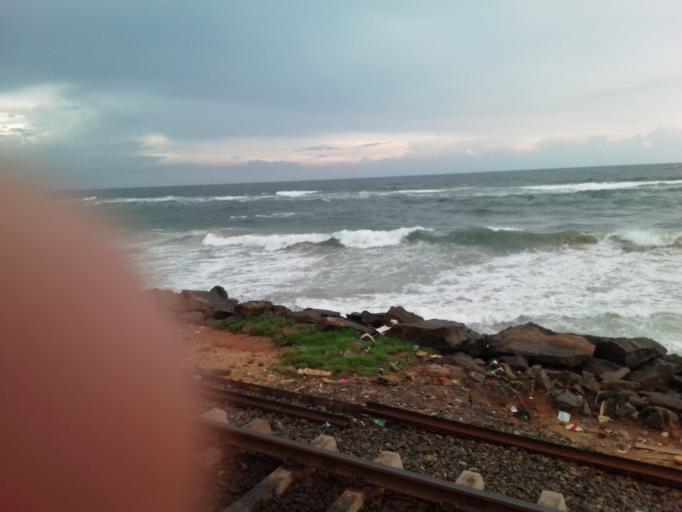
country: LK
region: Western
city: Colombo
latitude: 6.8928
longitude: 79.8532
